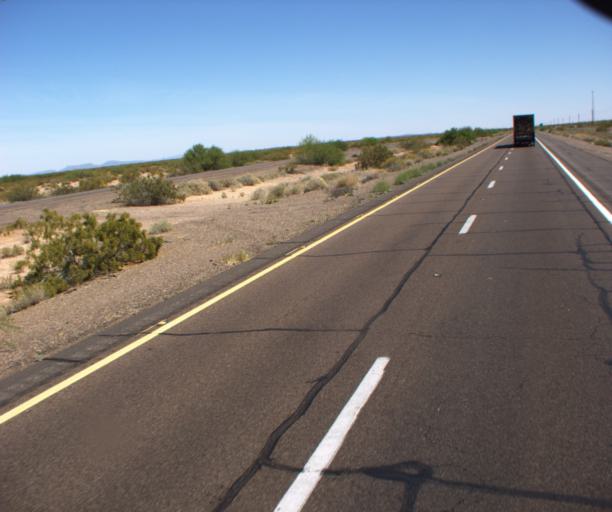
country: US
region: Arizona
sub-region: Maricopa County
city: Gila Bend
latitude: 32.8317
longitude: -113.3863
